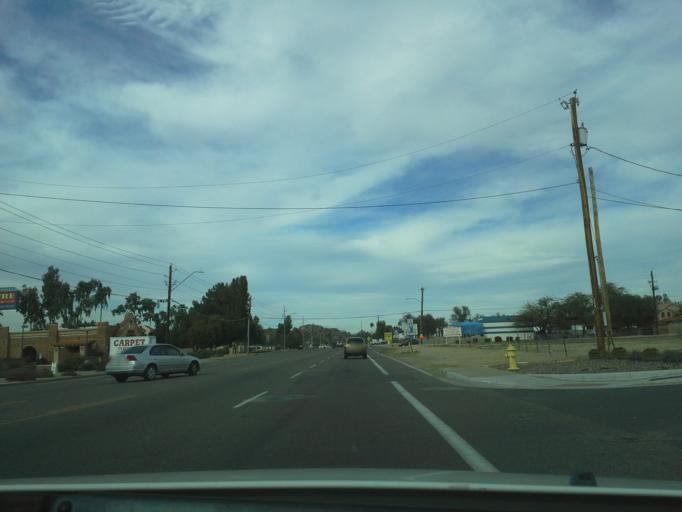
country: US
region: Arizona
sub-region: Maricopa County
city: Paradise Valley
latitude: 33.6447
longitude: -112.0308
